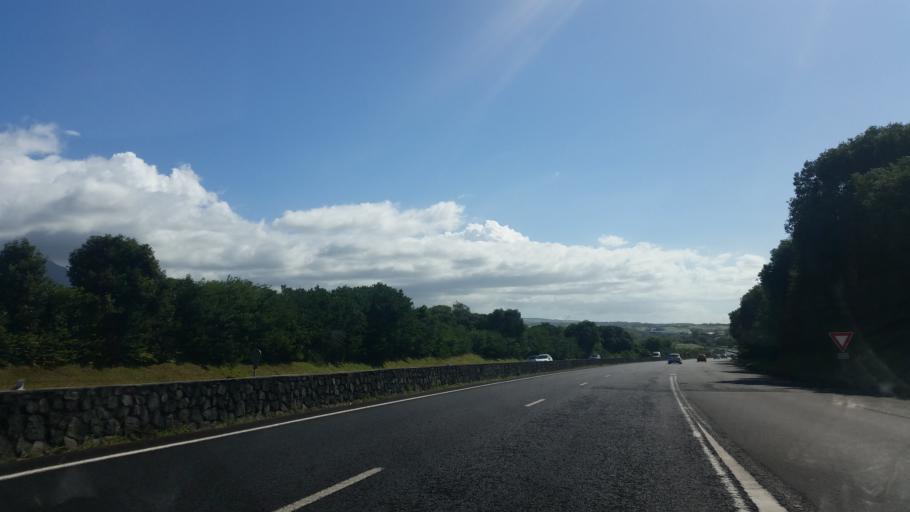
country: RE
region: Reunion
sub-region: Reunion
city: Bras-Panon
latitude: -21.0133
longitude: 55.6908
